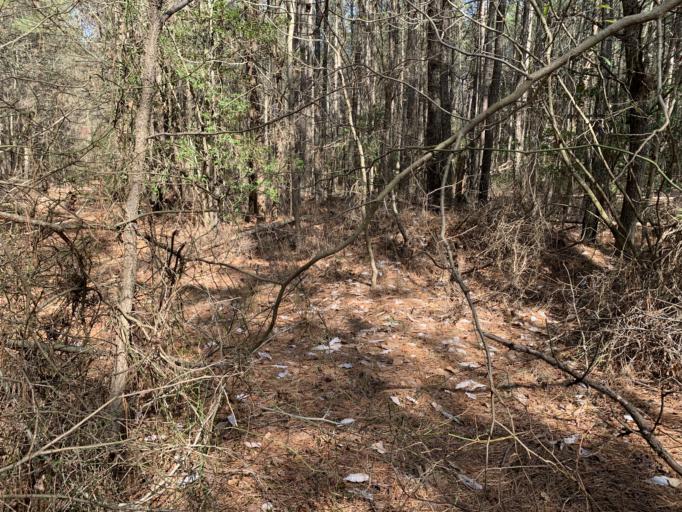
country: US
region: Delaware
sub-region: Sussex County
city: Georgetown
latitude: 38.6821
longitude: -75.4745
